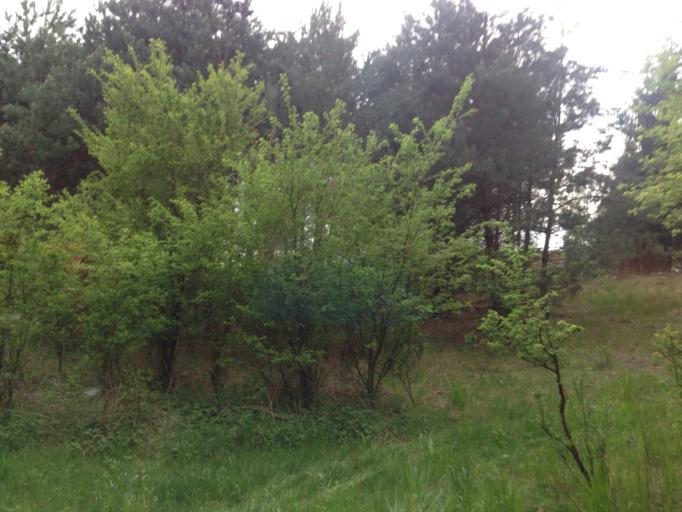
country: PL
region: Kujawsko-Pomorskie
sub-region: Powiat brodnicki
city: Bartniczka
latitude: 53.2813
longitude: 19.6585
